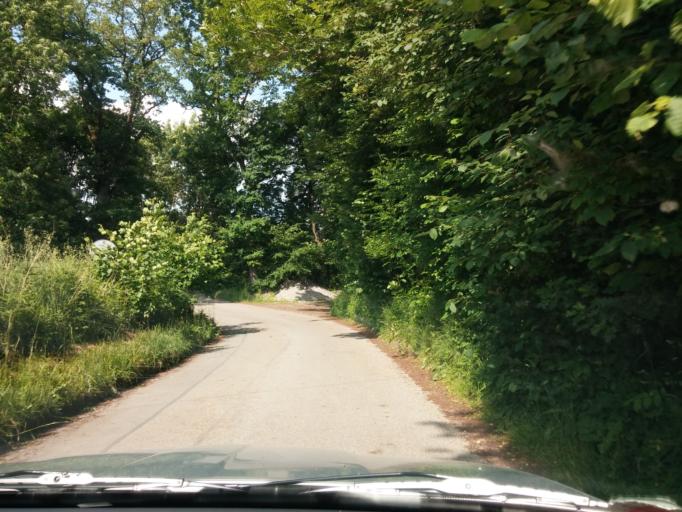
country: DE
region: Bavaria
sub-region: Swabia
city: Buxheim
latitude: 47.9640
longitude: 10.1199
